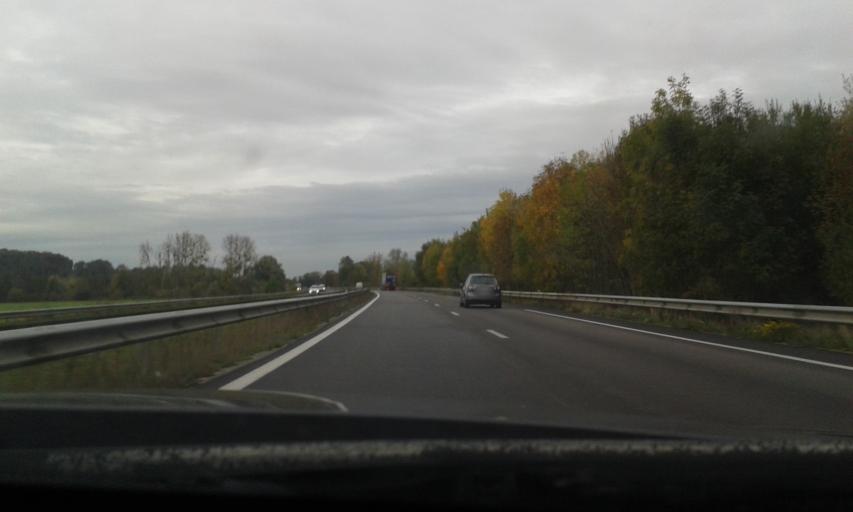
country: FR
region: Haute-Normandie
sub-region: Departement de l'Eure
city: Heudreville-sur-Eure
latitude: 49.1525
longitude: 1.1826
